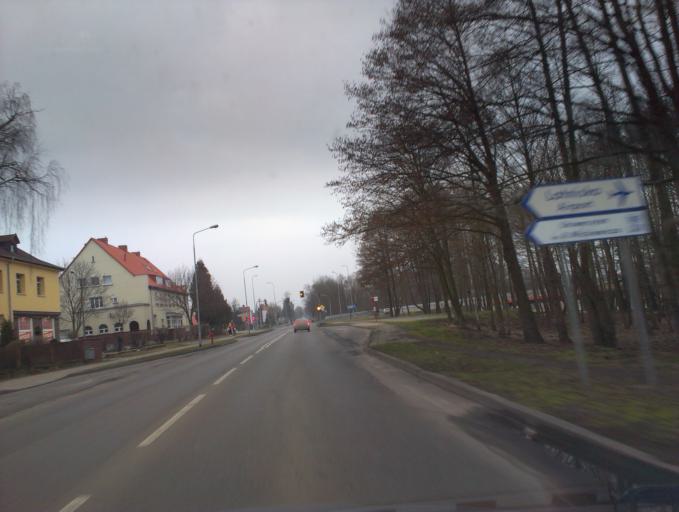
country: PL
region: Greater Poland Voivodeship
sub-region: Powiat pilski
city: Pila
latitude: 53.1615
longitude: 16.7375
